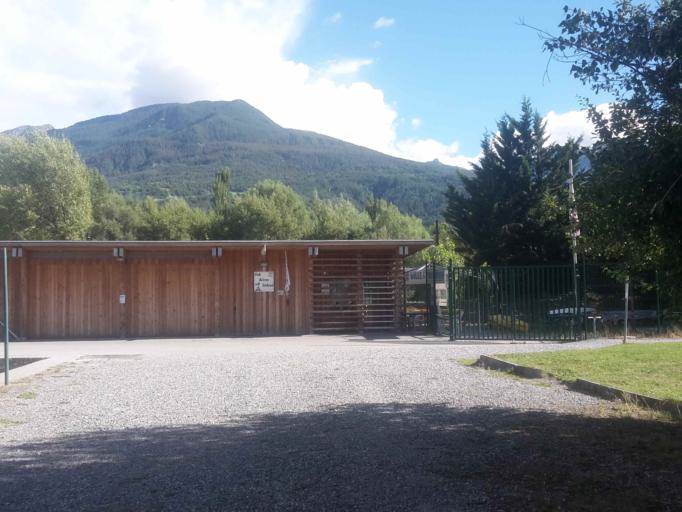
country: FR
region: Provence-Alpes-Cote d'Azur
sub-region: Departement des Hautes-Alpes
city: Embrun
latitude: 44.5490
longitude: 6.4780
